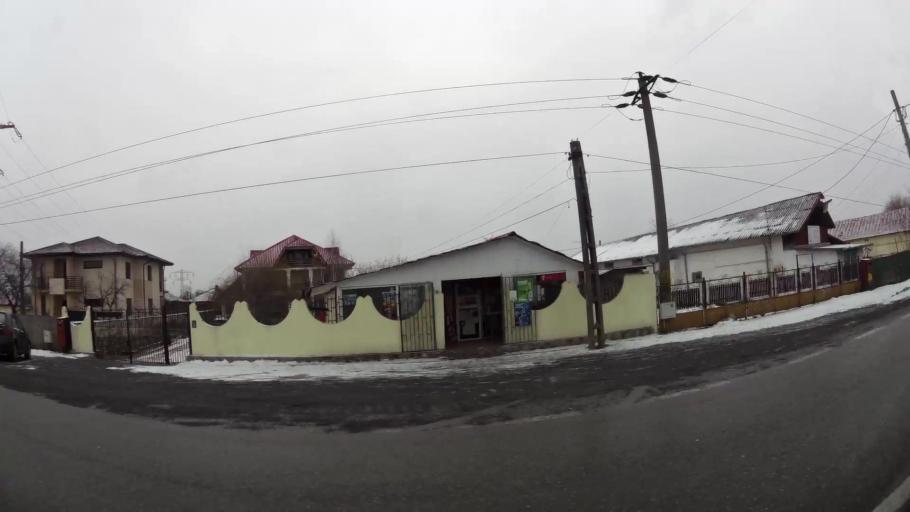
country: RO
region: Dambovita
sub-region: Comuna Aninoasa
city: Viforata
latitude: 44.9464
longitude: 25.4674
